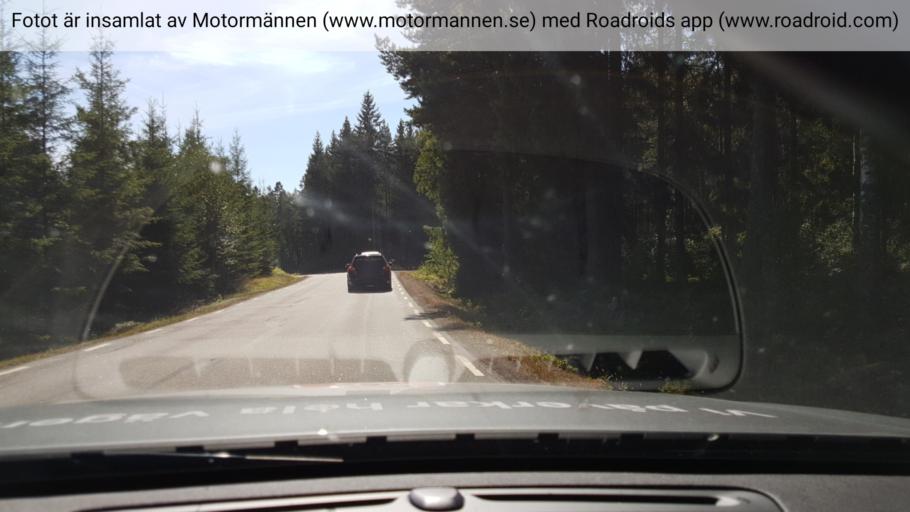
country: SE
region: Vaestra Goetaland
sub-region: Toreboda Kommun
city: Toereboda
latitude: 58.6742
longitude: 14.3102
